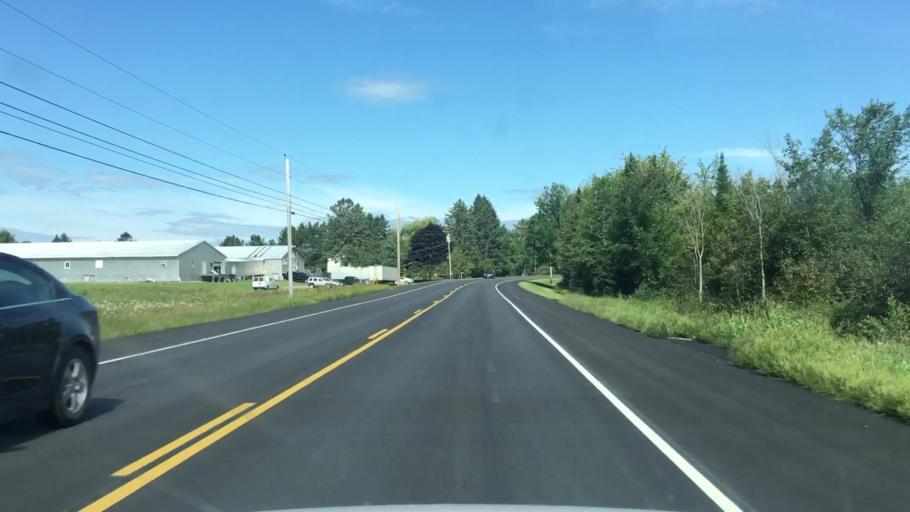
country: US
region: Maine
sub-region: Penobscot County
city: Corinna
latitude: 44.9676
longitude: -69.2742
